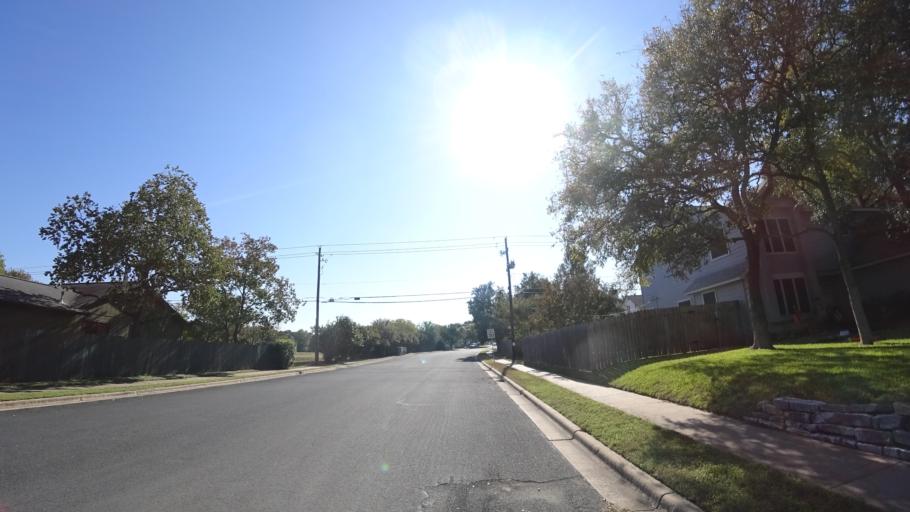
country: US
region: Texas
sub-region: Travis County
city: Shady Hollow
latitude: 30.2021
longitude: -97.8454
